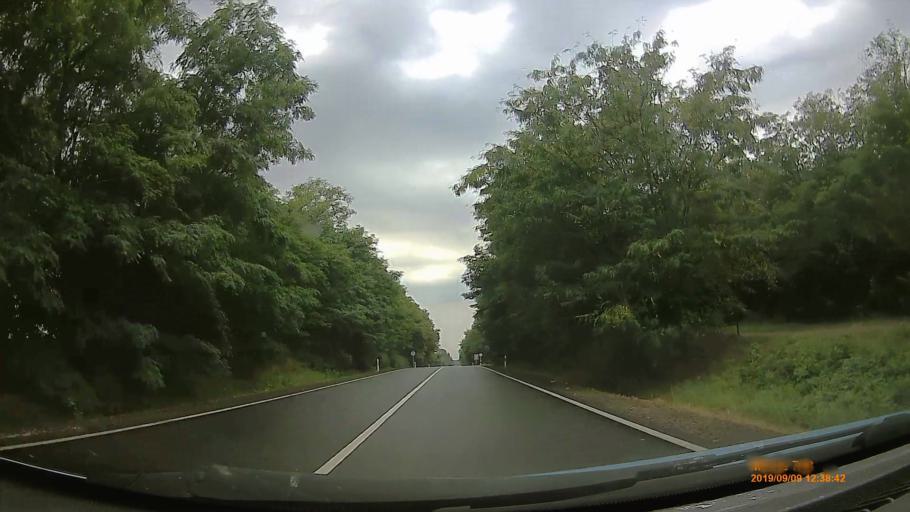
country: HU
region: Szabolcs-Szatmar-Bereg
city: Nyirpazony
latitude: 47.9944
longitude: 21.8064
